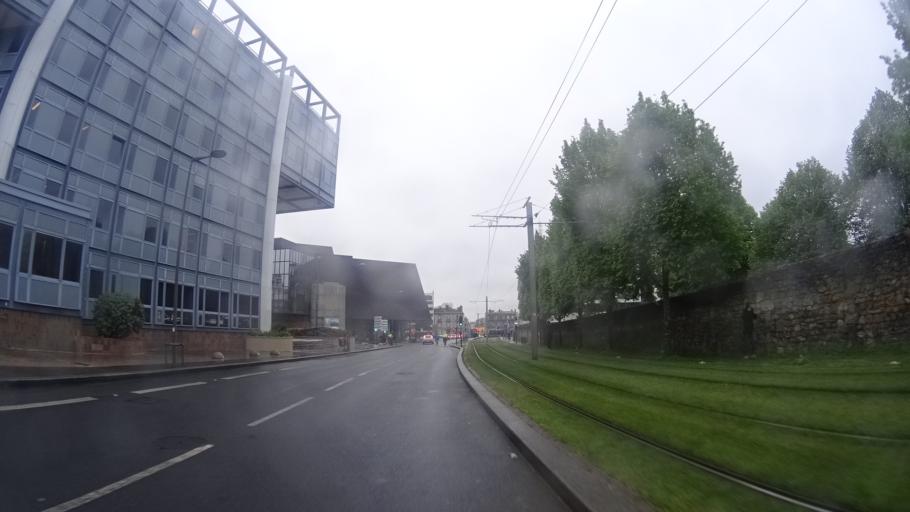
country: FR
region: Aquitaine
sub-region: Departement de la Gironde
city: Bordeaux
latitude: 44.8362
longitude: -0.5890
